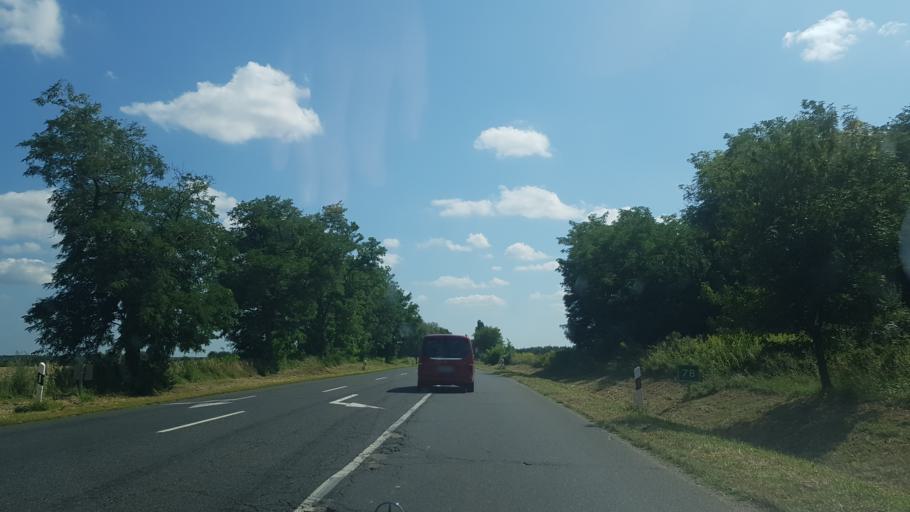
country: HU
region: Somogy
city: Marcali
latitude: 46.5539
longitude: 17.4118
